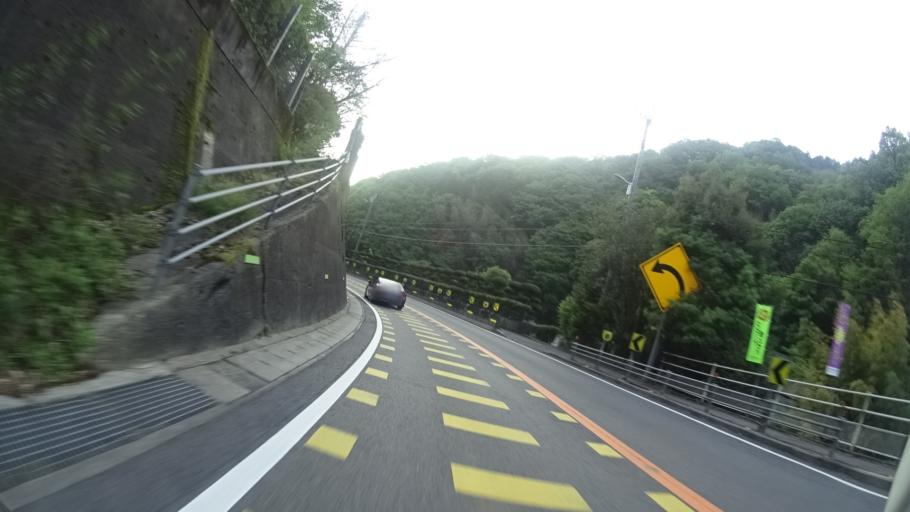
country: JP
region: Ehime
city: Kawanoecho
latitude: 33.9965
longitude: 133.6671
